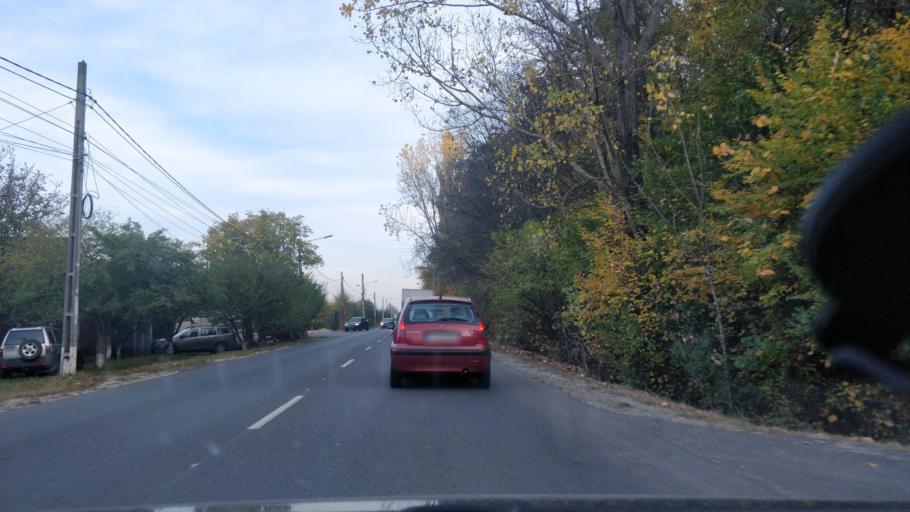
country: RO
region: Ilfov
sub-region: Comuna Ciorogarla
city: Ciorogarla
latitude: 44.4463
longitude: 25.8568
